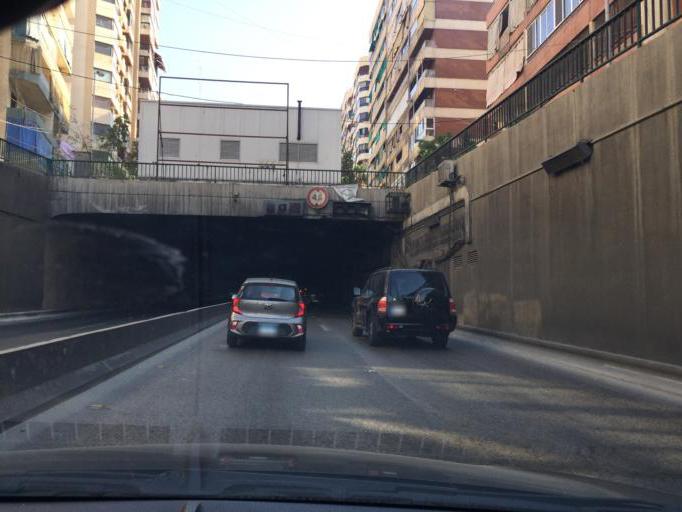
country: LB
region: Beyrouth
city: Beirut
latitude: 33.8878
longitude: 35.4991
